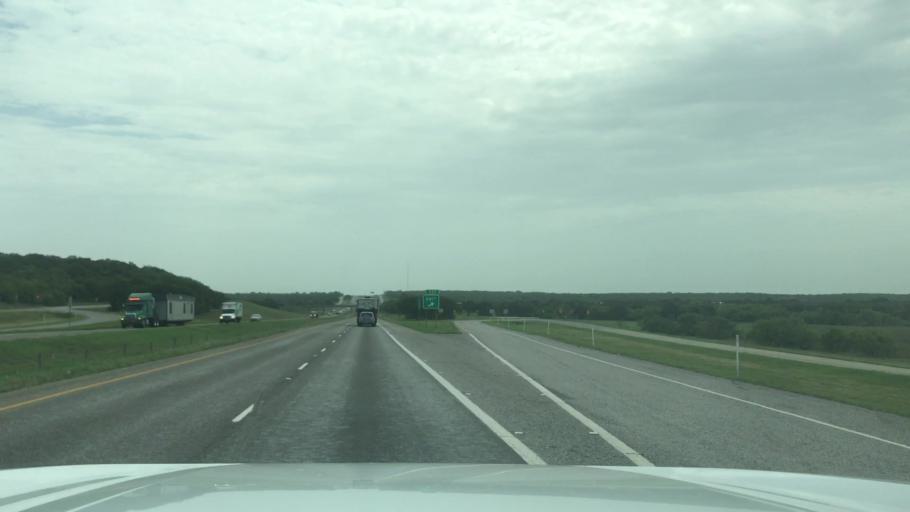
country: US
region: Texas
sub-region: Eastland County
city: Eastland
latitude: 32.3754
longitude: -98.8949
